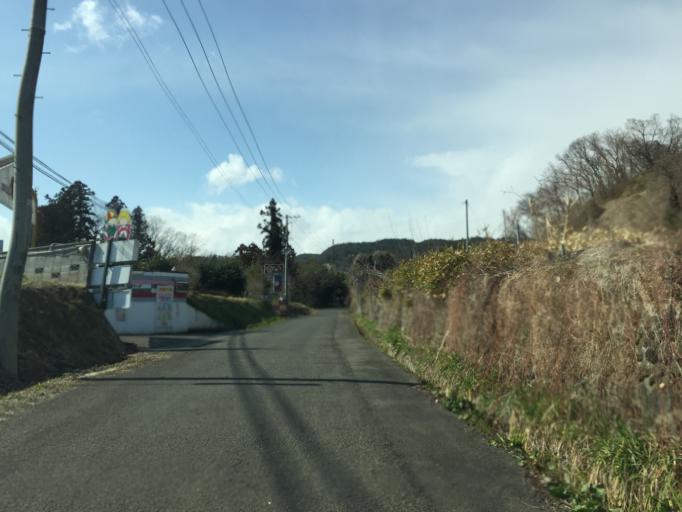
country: JP
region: Fukushima
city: Fukushima-shi
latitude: 37.8250
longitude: 140.4236
